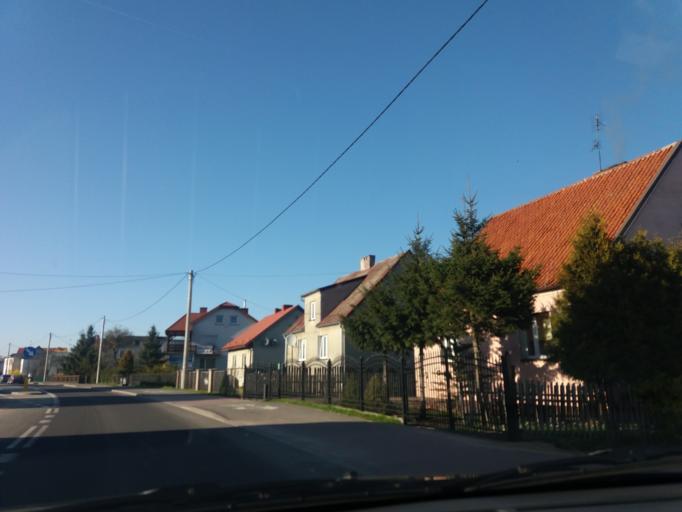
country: PL
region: Warmian-Masurian Voivodeship
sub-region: Powiat nidzicki
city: Nidzica
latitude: 53.3683
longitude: 20.4298
